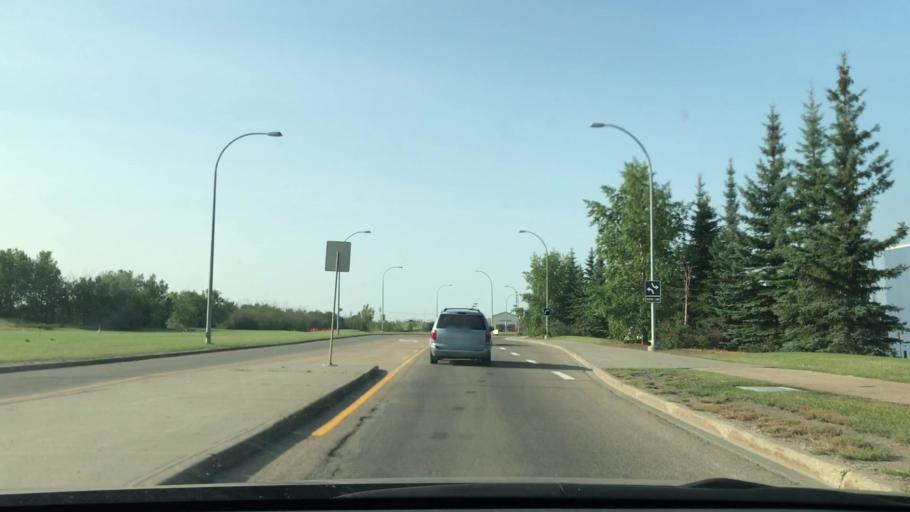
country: CA
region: Alberta
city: Edmonton
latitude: 53.4457
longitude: -113.4807
